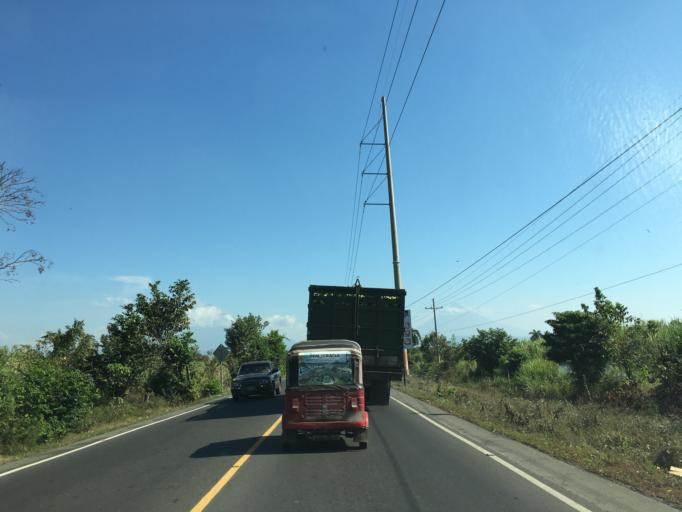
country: GT
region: Escuintla
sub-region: Municipio de La Democracia
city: La Democracia
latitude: 14.2130
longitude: -90.9558
